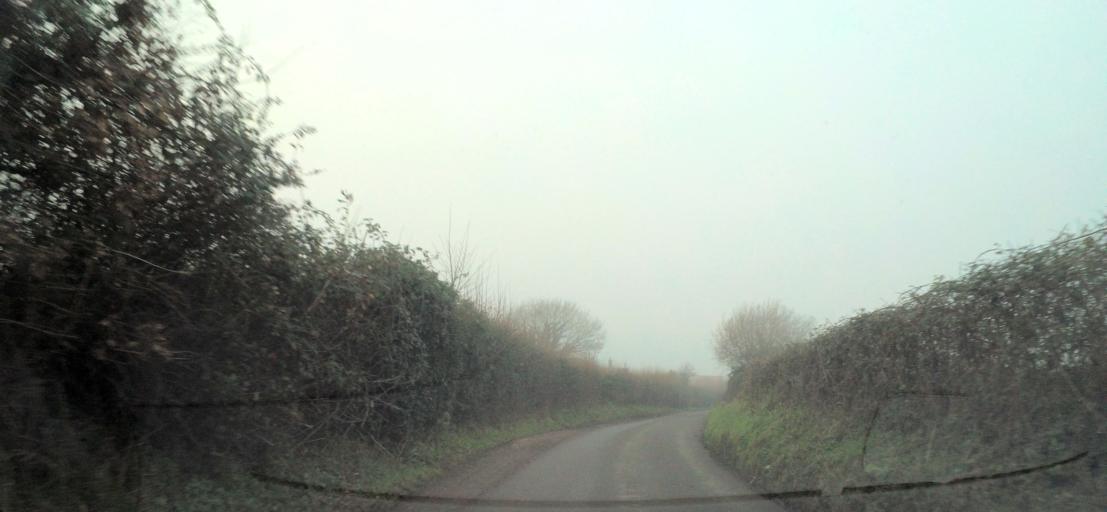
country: GB
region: England
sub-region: West Berkshire
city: Theale
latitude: 51.4062
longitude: -1.0971
